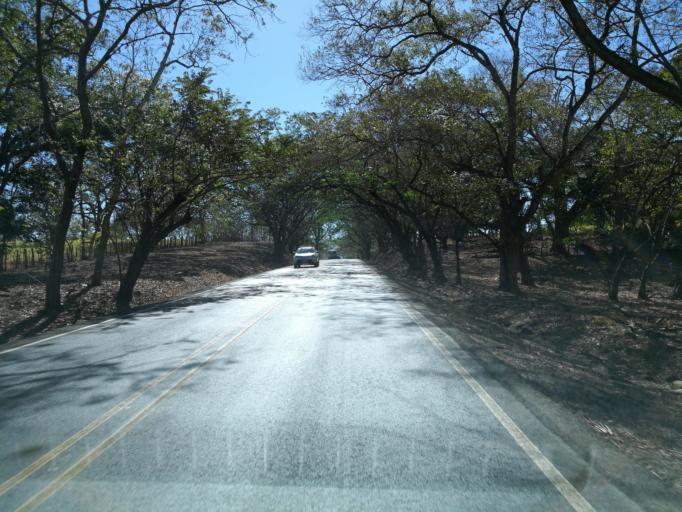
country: CR
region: Puntarenas
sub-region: Canton Central de Puntarenas
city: Puntarenas
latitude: 10.1063
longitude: -84.8807
